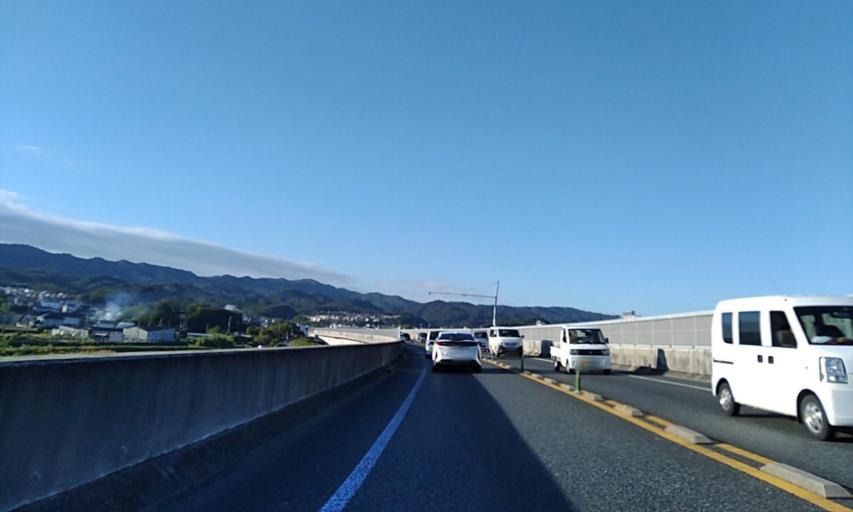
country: JP
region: Wakayama
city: Iwade
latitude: 34.3507
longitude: 135.2575
